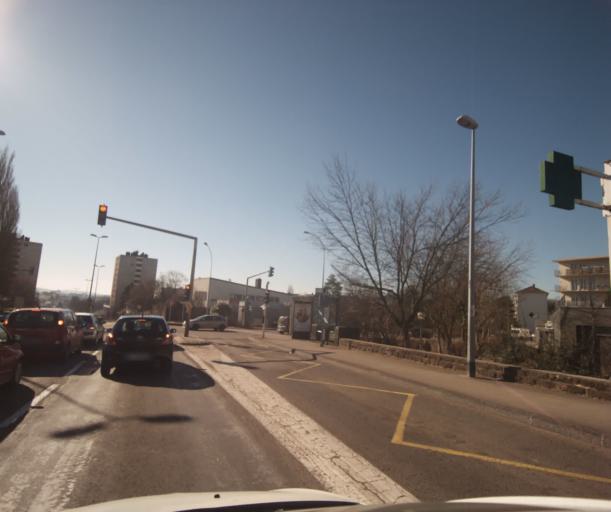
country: FR
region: Franche-Comte
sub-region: Departement du Doubs
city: Besancon
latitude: 47.2477
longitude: 5.9993
